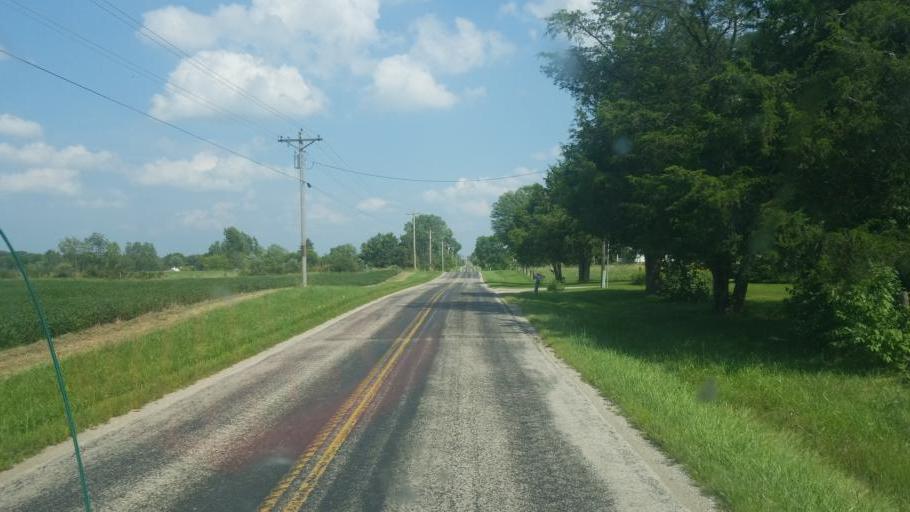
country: US
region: Ohio
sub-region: Huron County
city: New London
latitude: 41.0579
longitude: -82.2968
